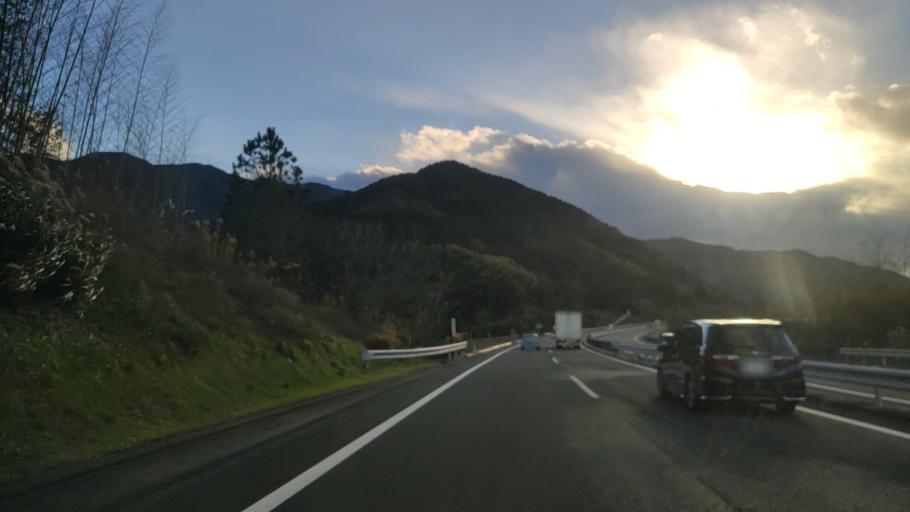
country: JP
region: Ehime
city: Saijo
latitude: 33.8671
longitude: 133.0579
